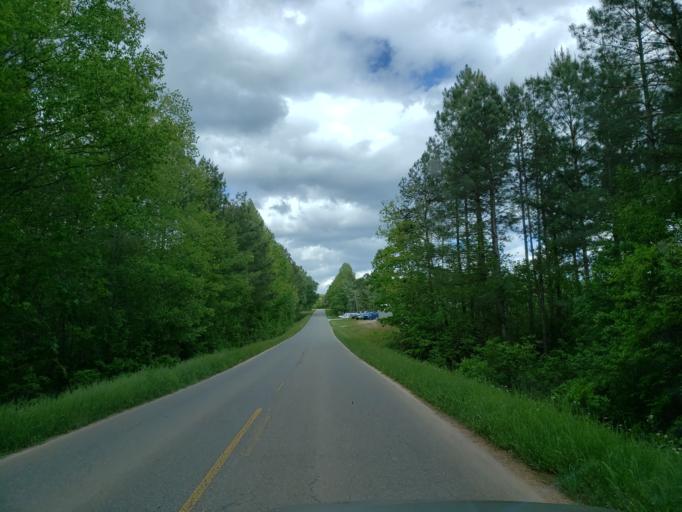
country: US
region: Georgia
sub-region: Haralson County
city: Tallapoosa
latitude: 33.6923
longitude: -85.3551
